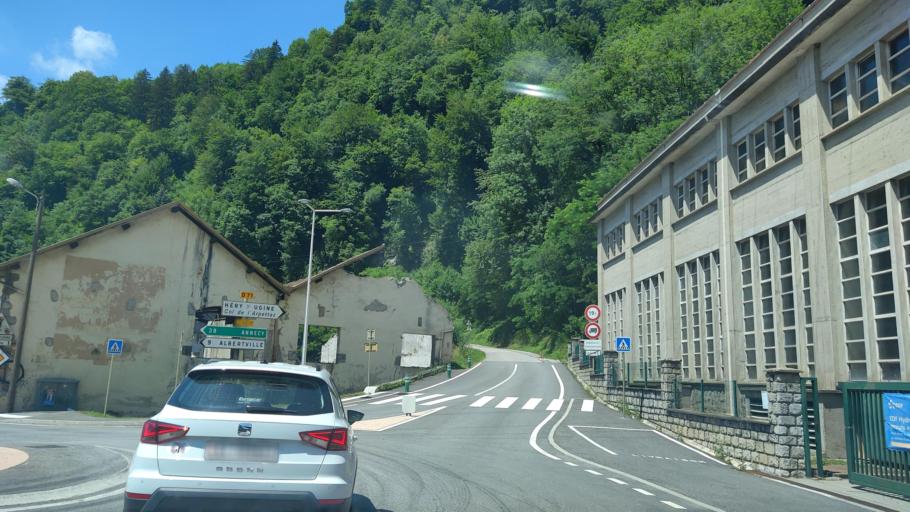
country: FR
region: Rhone-Alpes
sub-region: Departement de la Savoie
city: Ugine
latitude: 45.7516
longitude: 6.4347
